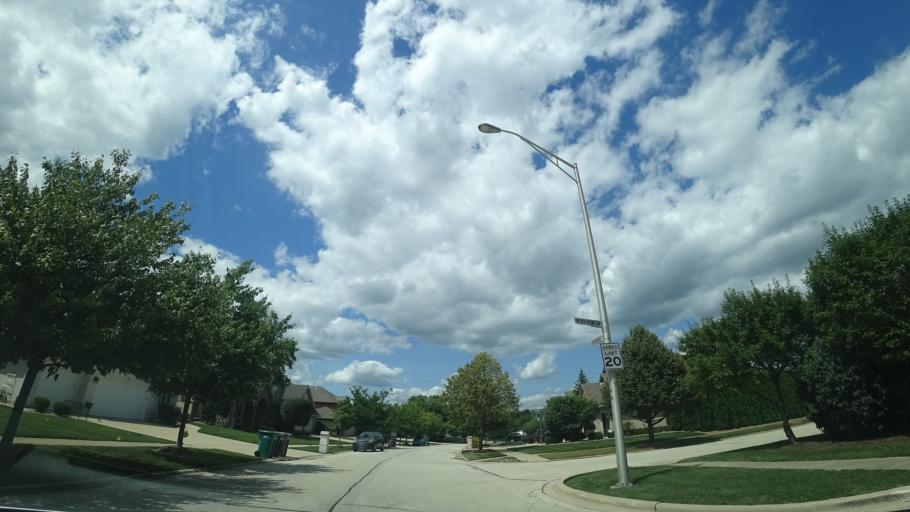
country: US
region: Illinois
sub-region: Will County
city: Homer Glen
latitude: 41.5821
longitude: -87.8970
